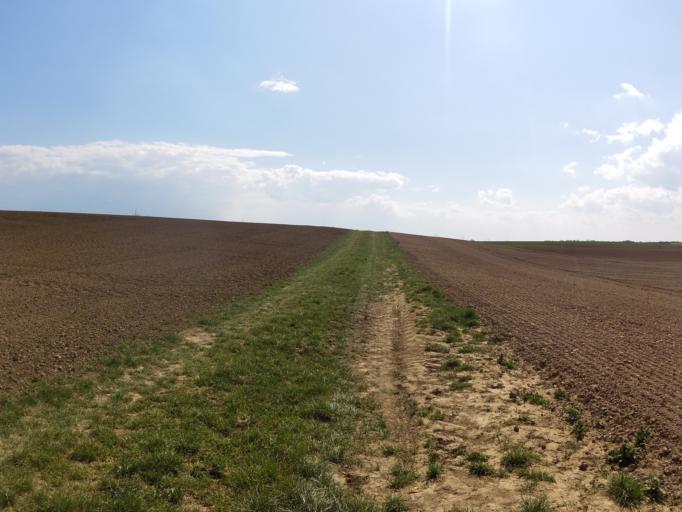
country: DE
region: Bavaria
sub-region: Regierungsbezirk Unterfranken
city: Oberpleichfeld
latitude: 49.8434
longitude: 10.0828
